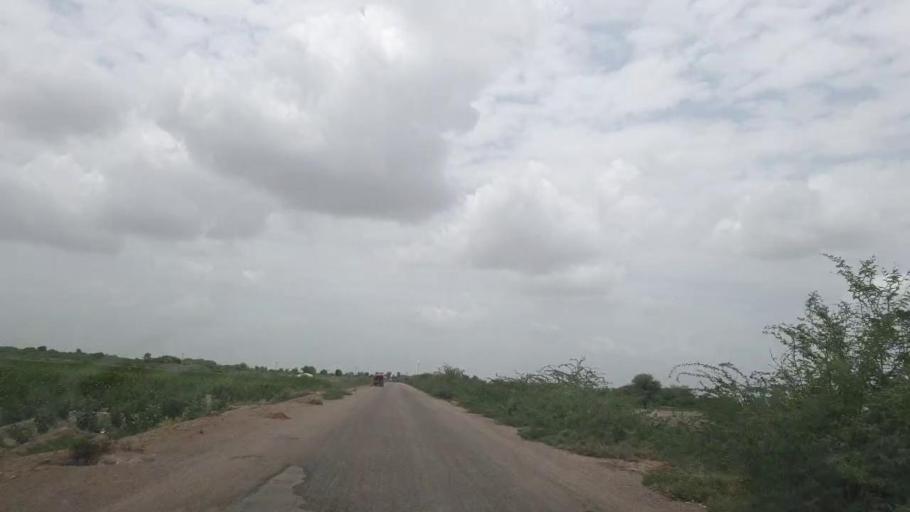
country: PK
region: Sindh
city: Naukot
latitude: 24.9199
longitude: 69.2728
